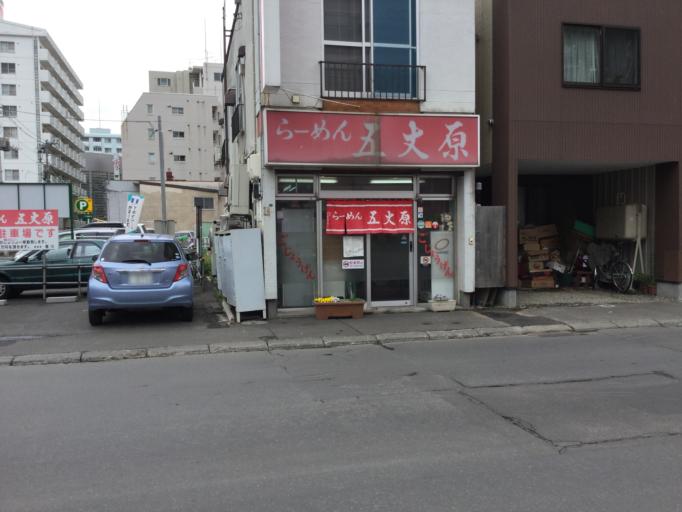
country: JP
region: Hokkaido
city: Sapporo
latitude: 43.0510
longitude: 141.3458
